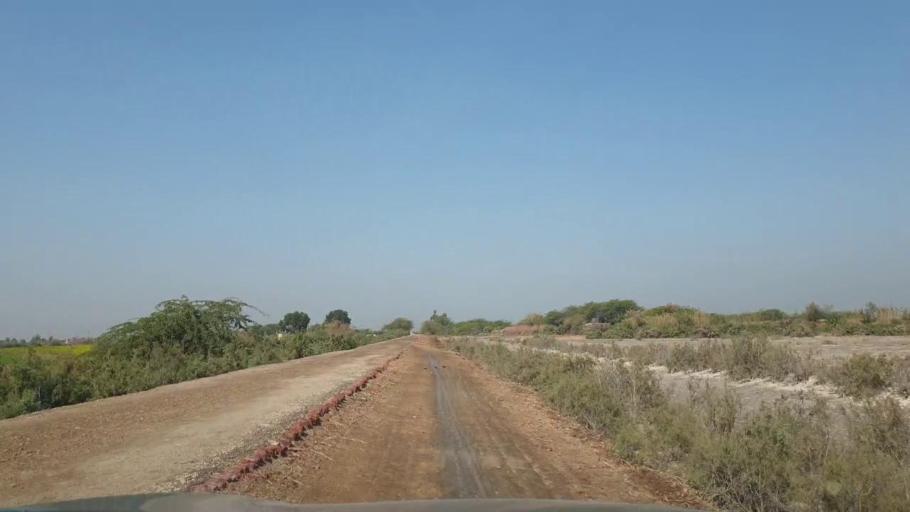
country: PK
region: Sindh
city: Berani
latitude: 25.6931
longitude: 68.8783
